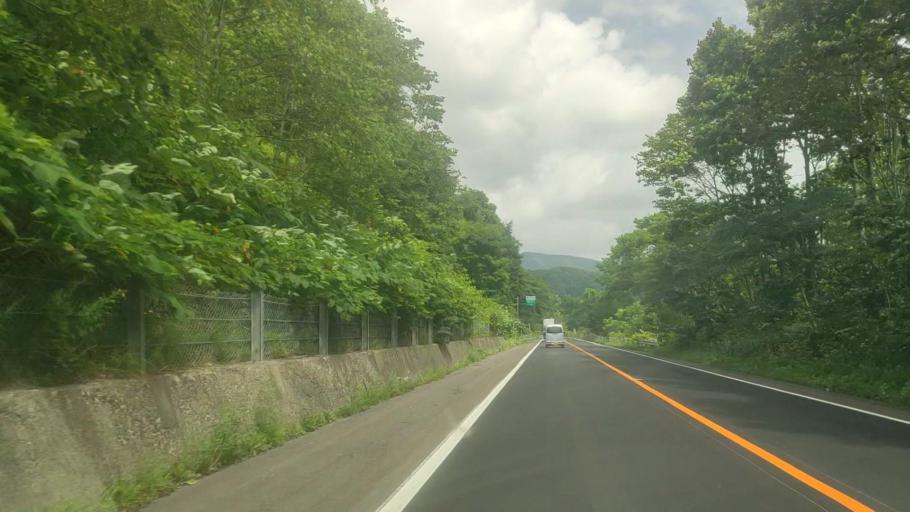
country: JP
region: Hokkaido
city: Niseko Town
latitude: 42.5981
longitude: 140.6047
